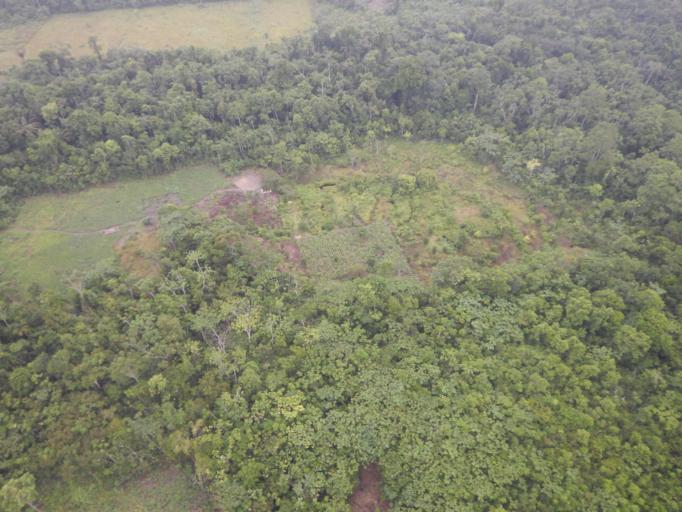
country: BO
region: Cochabamba
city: Chimore
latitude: -17.1811
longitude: -64.6486
